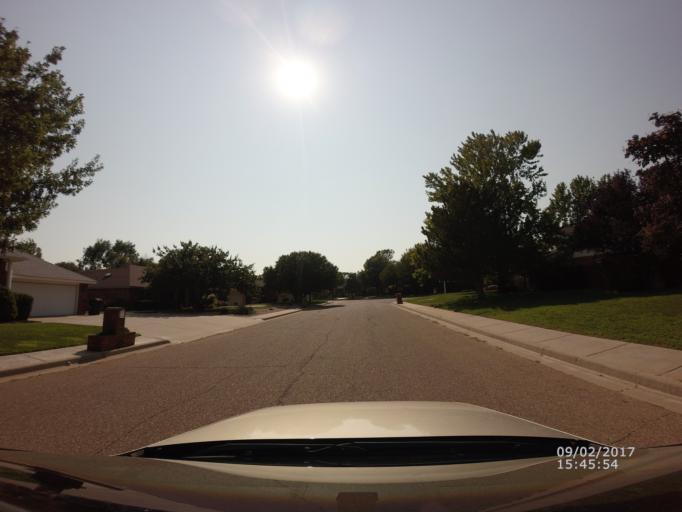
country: US
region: New Mexico
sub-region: Curry County
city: Clovis
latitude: 34.4445
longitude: -103.1850
